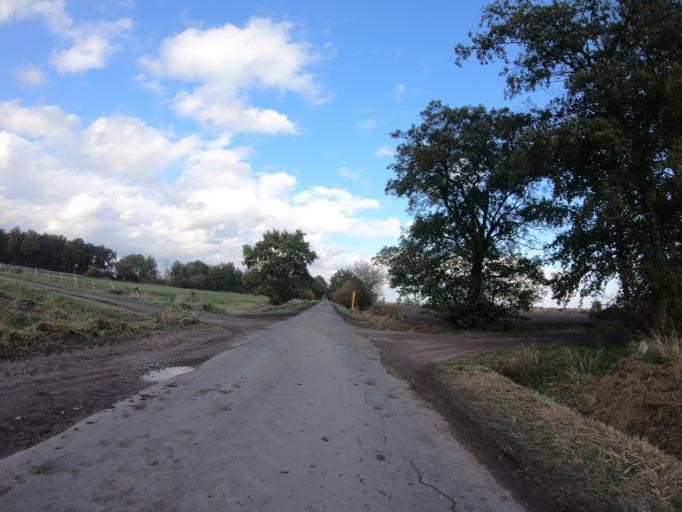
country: DE
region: Lower Saxony
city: Wagenhoff
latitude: 52.5290
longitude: 10.5437
